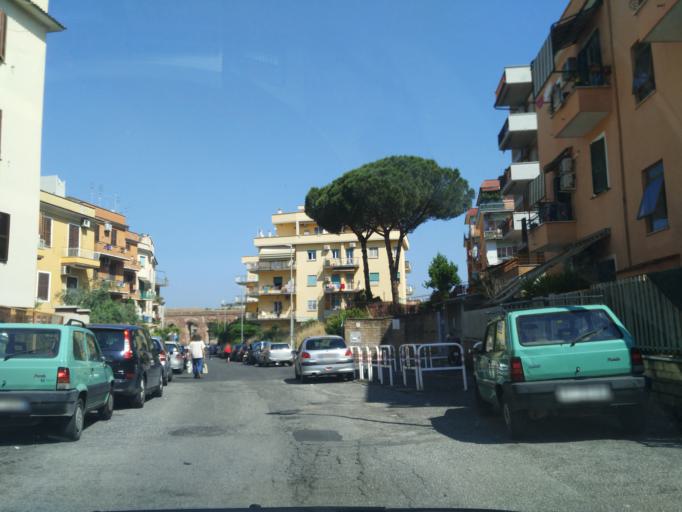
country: IT
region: Latium
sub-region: Citta metropolitana di Roma Capitale
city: Rome
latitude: 41.8773
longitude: 12.5755
